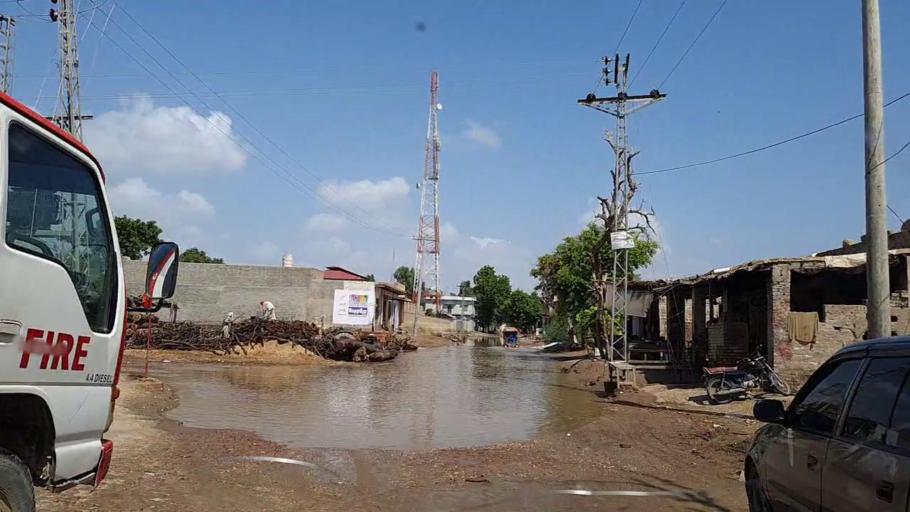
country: PK
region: Sindh
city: Pad Idan
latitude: 26.7758
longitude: 68.2962
